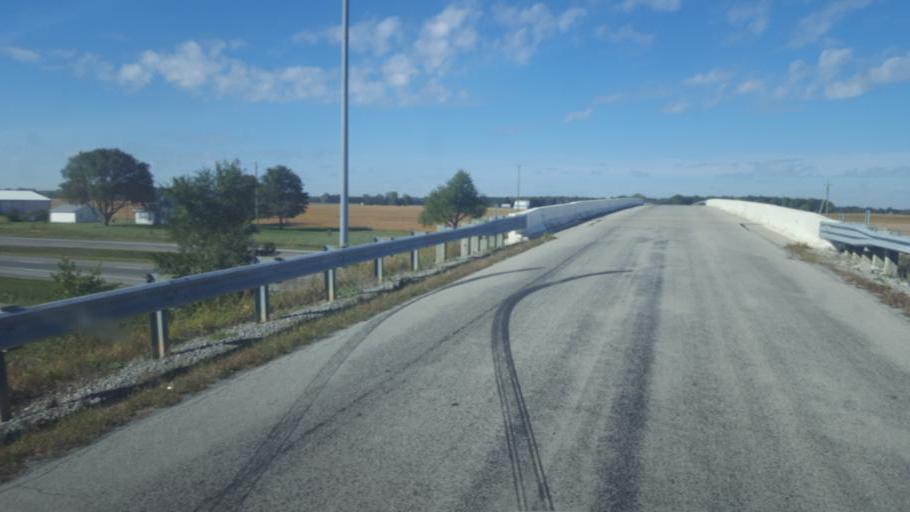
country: US
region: Ohio
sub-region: Wyandot County
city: Upper Sandusky
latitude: 40.8037
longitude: -83.2351
